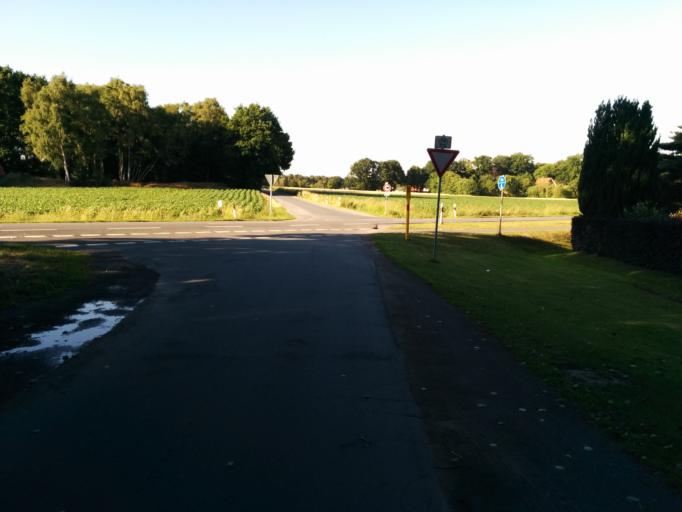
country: DE
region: Lower Saxony
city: Lohne
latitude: 52.6615
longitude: 8.2680
